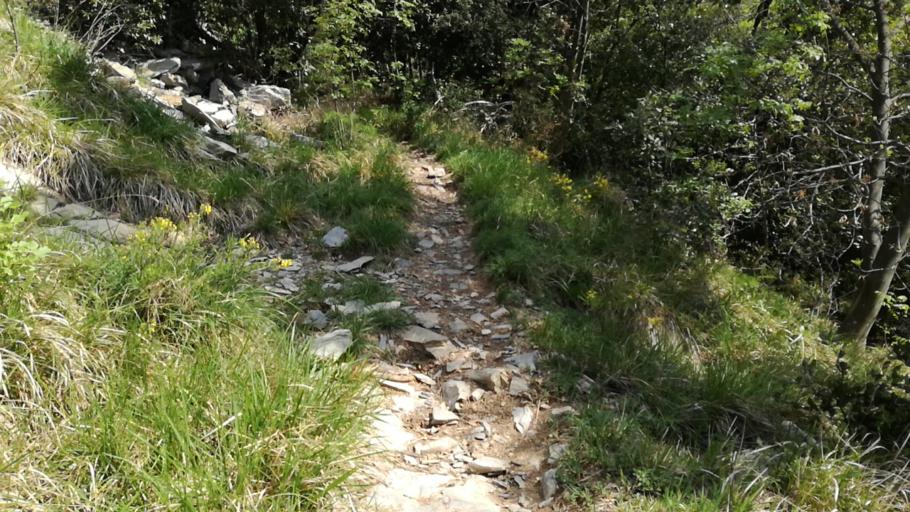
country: IT
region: Liguria
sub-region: Provincia di Genova
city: Genoa
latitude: 44.4377
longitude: 8.9274
